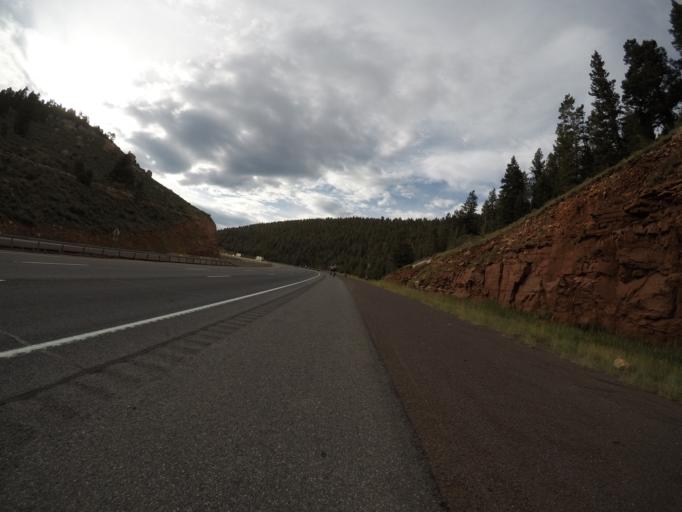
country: US
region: Wyoming
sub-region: Albany County
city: Laramie
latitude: 41.2670
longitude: -105.4766
